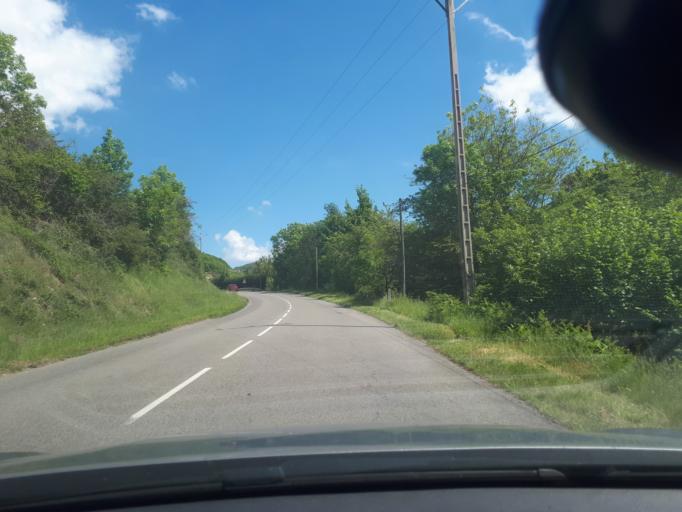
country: FR
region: Rhone-Alpes
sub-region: Departement du Rhone
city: Aveize
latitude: 45.6945
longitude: 4.4931
